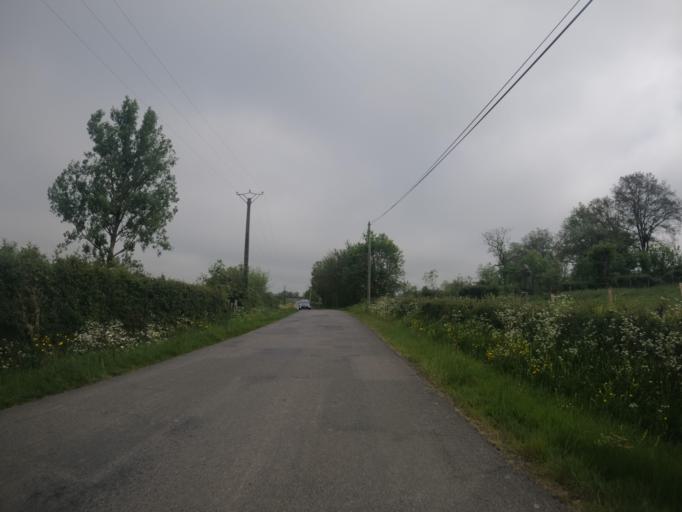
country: FR
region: Poitou-Charentes
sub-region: Departement des Deux-Sevres
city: Chiche
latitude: 46.8309
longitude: -0.3761
